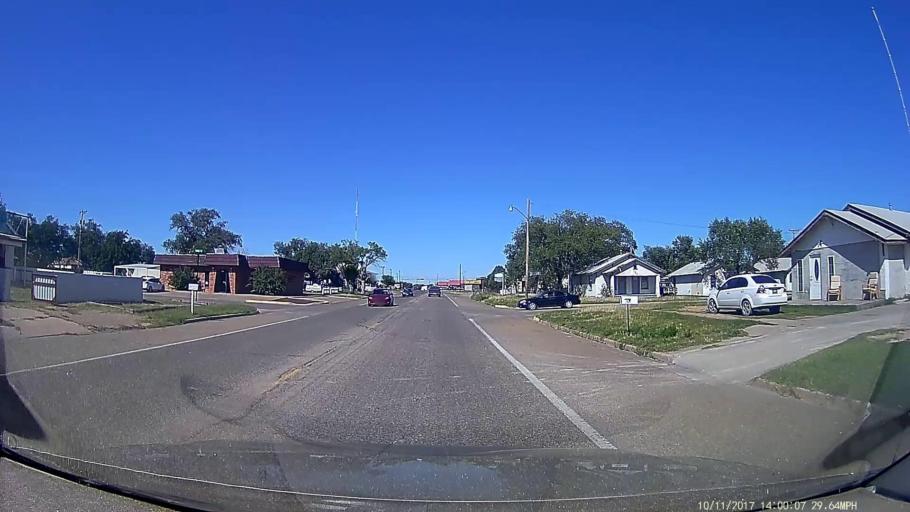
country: US
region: New Mexico
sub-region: Curry County
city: Clovis
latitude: 34.4098
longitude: -103.2066
